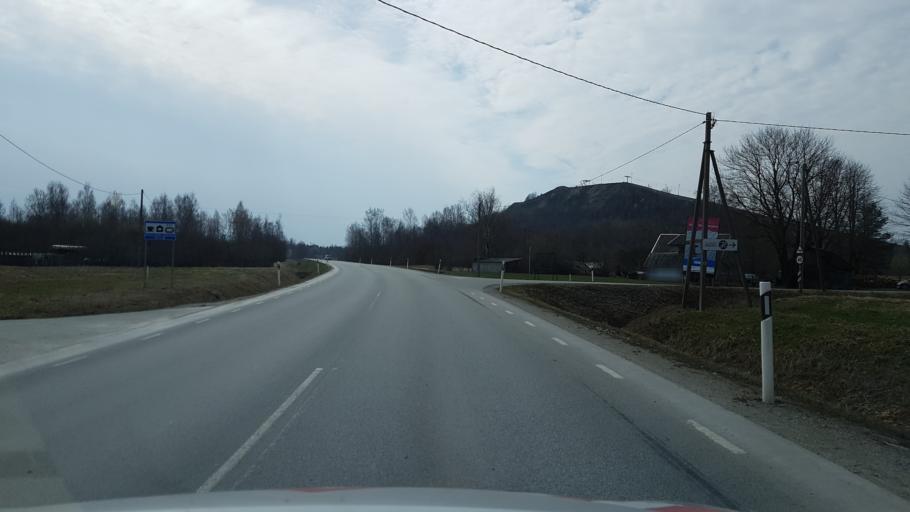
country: EE
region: Ida-Virumaa
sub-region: Kivioli linn
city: Kivioli
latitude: 59.3651
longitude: 26.9657
